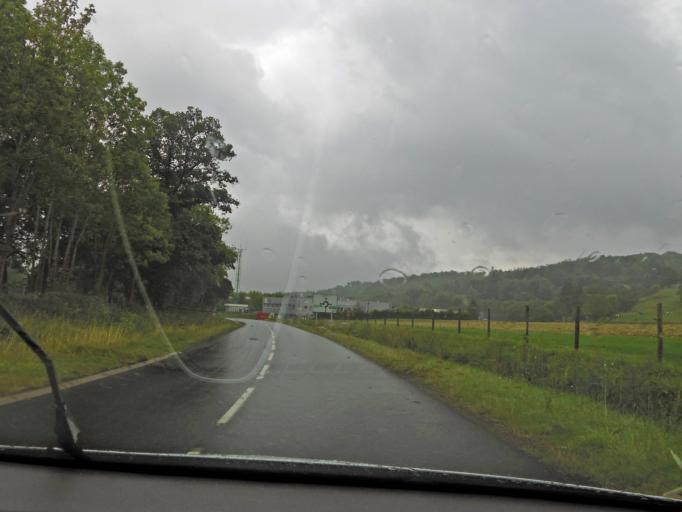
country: FR
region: Auvergne
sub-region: Departement du Puy-de-Dome
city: Saint-Genes-Champanelle
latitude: 45.7054
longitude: 3.0141
